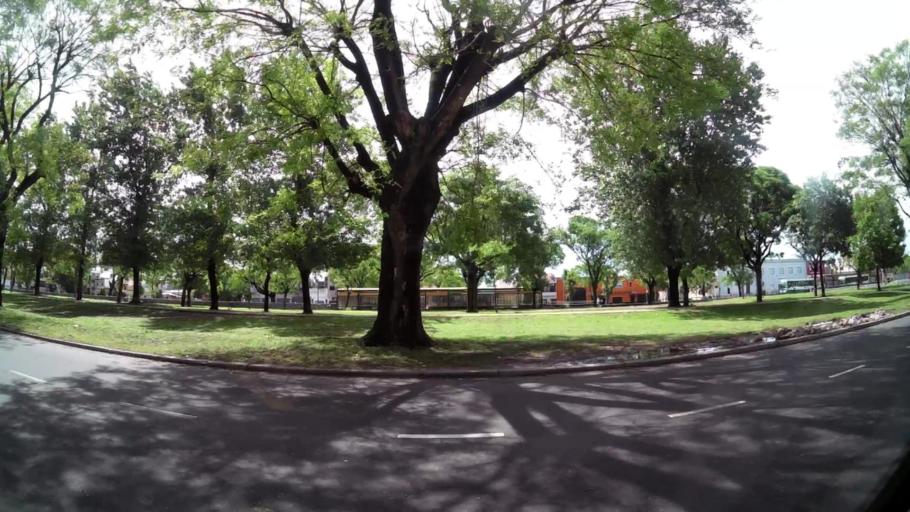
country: AR
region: Buenos Aires F.D.
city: Villa Lugano
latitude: -34.6606
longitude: -58.4291
